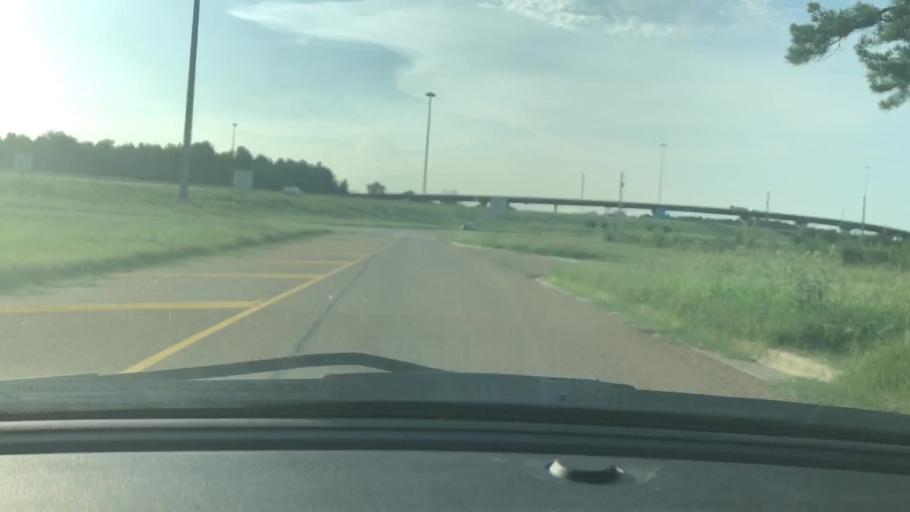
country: US
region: Texas
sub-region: Bowie County
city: Wake Village
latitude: 33.3899
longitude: -94.0960
